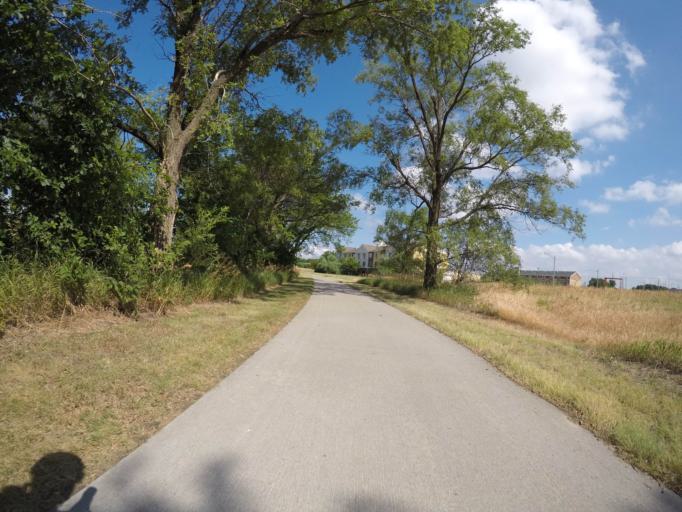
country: US
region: Nebraska
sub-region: Buffalo County
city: Kearney
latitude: 40.6755
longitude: -99.0876
